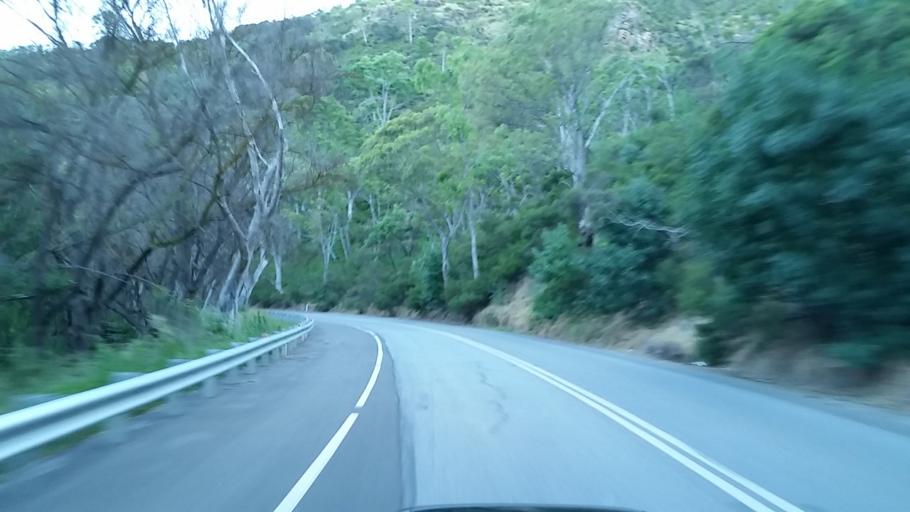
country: AU
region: South Australia
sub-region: Campbelltown
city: Athelstone
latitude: -34.8612
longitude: 138.7413
